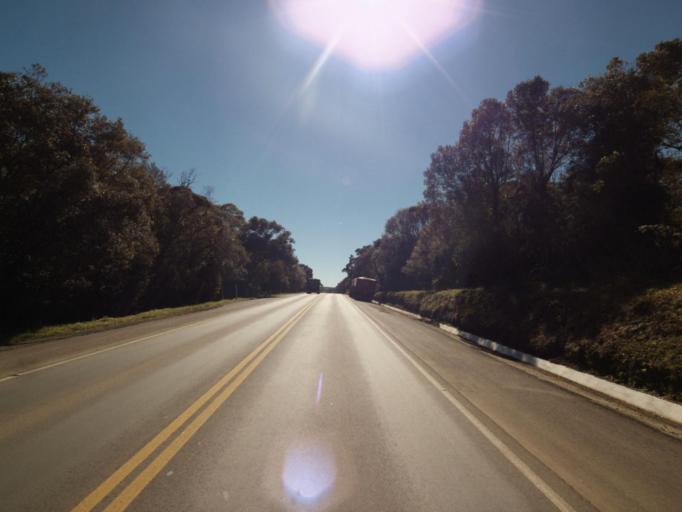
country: BR
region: Santa Catarina
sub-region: Concordia
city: Concordia
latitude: -26.9632
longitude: -51.8549
